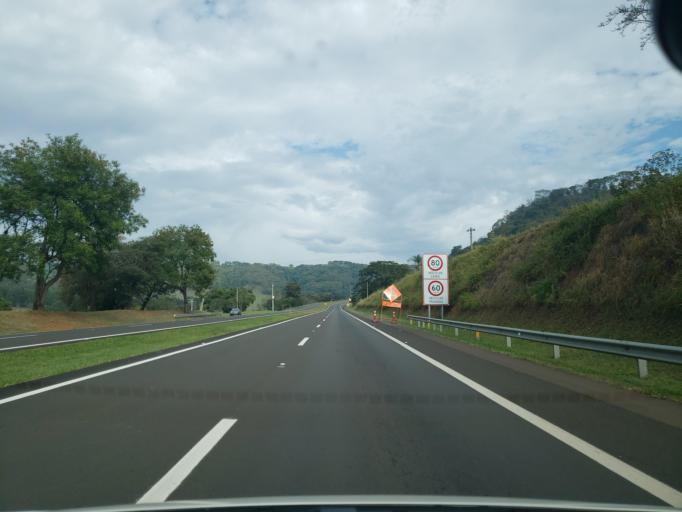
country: BR
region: Sao Paulo
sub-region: Dois Corregos
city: Dois Corregos
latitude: -22.2475
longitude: -48.3323
